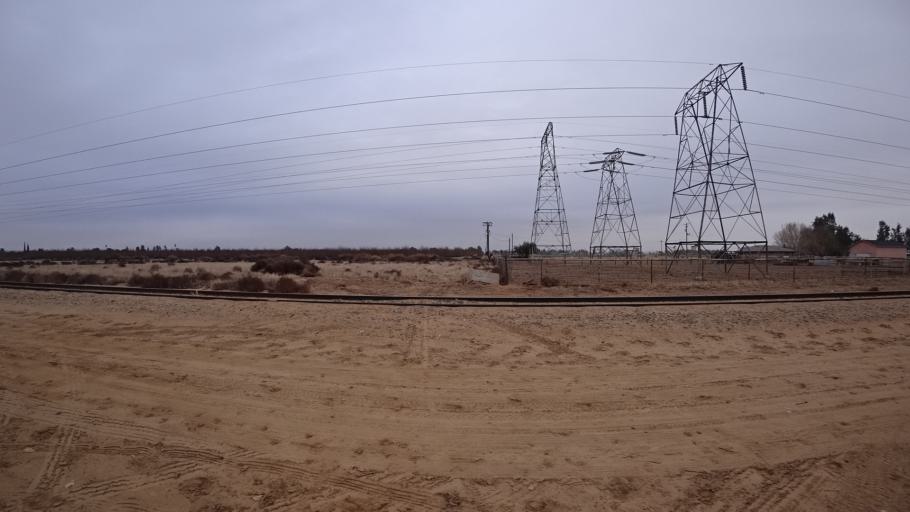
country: US
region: California
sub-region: Kern County
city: Lamont
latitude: 35.3325
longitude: -118.9234
